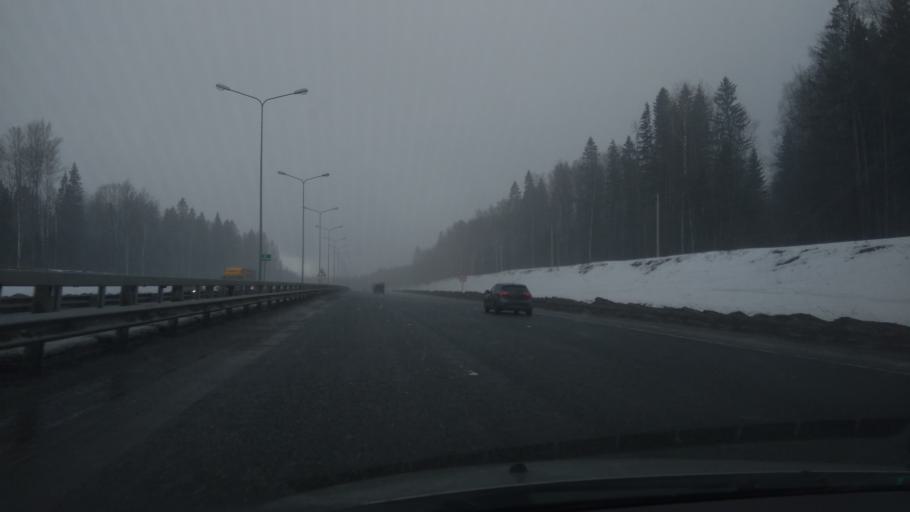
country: RU
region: Perm
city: Zvezdnyy
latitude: 57.7575
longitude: 56.3336
